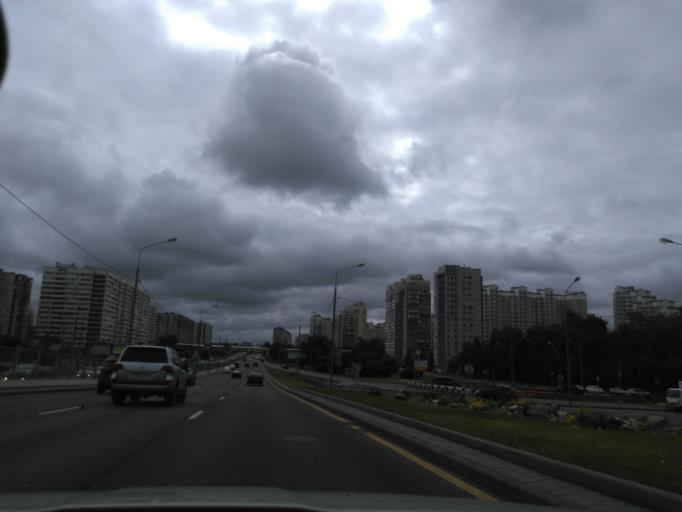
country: RU
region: Moskovskaya
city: Bol'shaya Setun'
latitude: 55.7453
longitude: 37.4210
